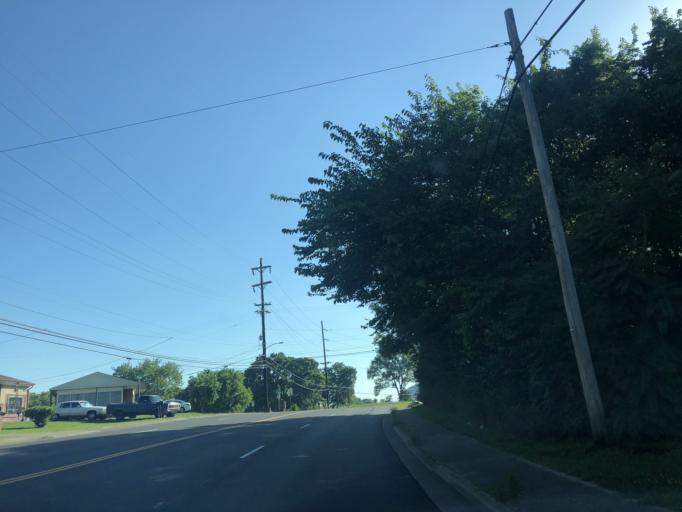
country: US
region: Tennessee
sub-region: Davidson County
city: Nashville
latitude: 36.1830
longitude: -86.8448
